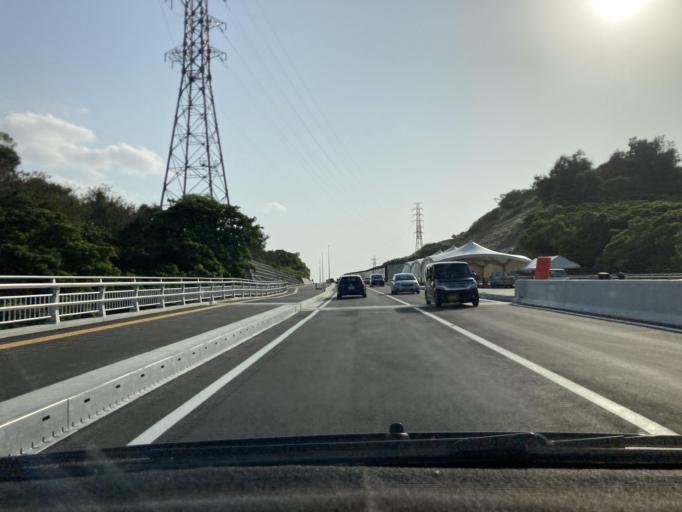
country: JP
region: Okinawa
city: Ginowan
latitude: 26.2080
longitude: 127.7521
